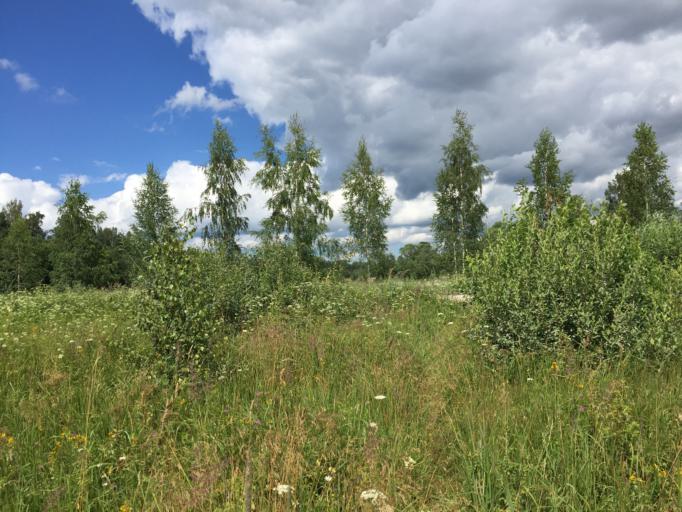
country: LV
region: Ropazu
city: Ropazi
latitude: 56.9087
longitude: 24.7707
